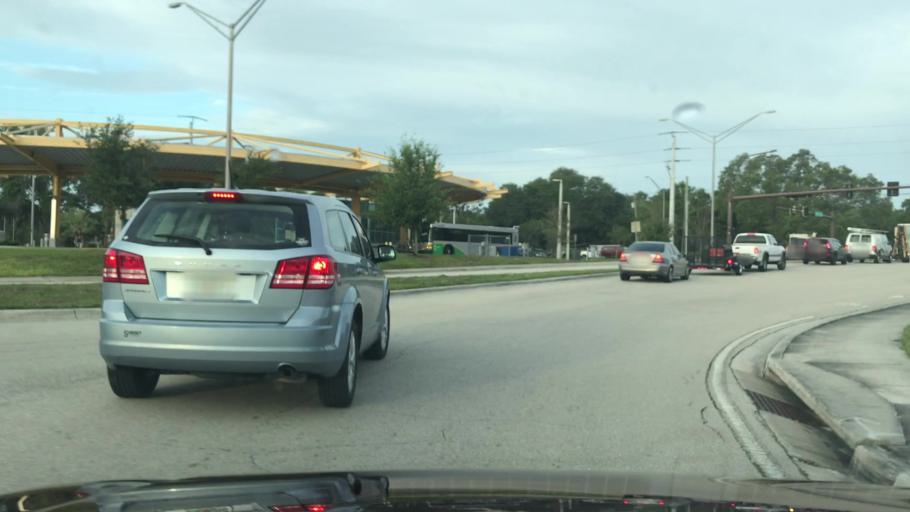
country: US
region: Florida
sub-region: Sarasota County
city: Fruitville
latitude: 27.3232
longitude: -82.4503
